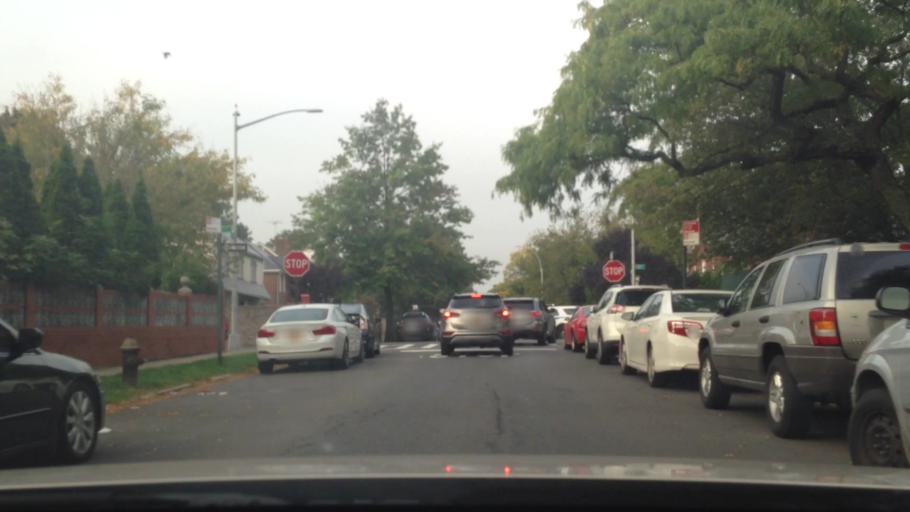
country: US
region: New York
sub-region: Queens County
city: Borough of Queens
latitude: 40.7291
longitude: -73.8447
